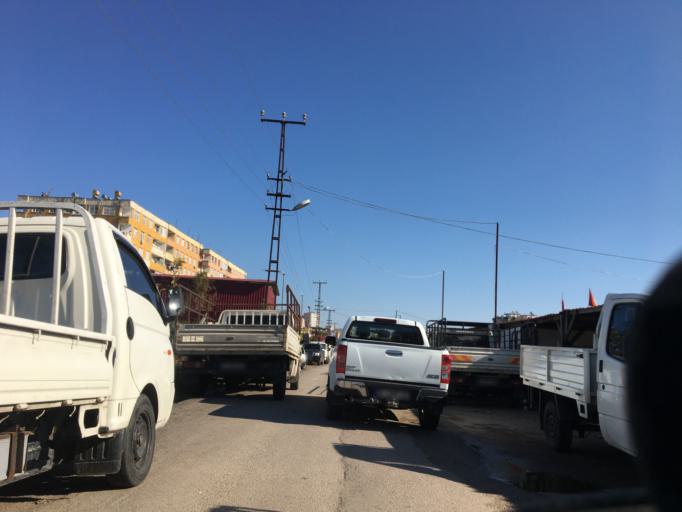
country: TR
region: Adana
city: Seyhan
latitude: 37.0116
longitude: 35.2964
